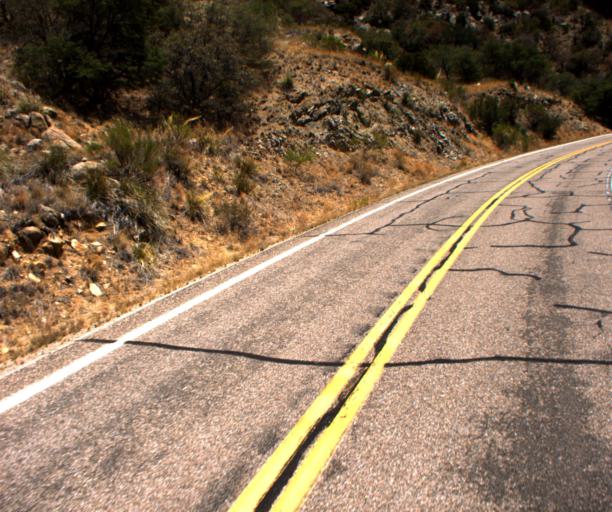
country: US
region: Arizona
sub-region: Pima County
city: Sells
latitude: 31.9681
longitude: -111.6206
